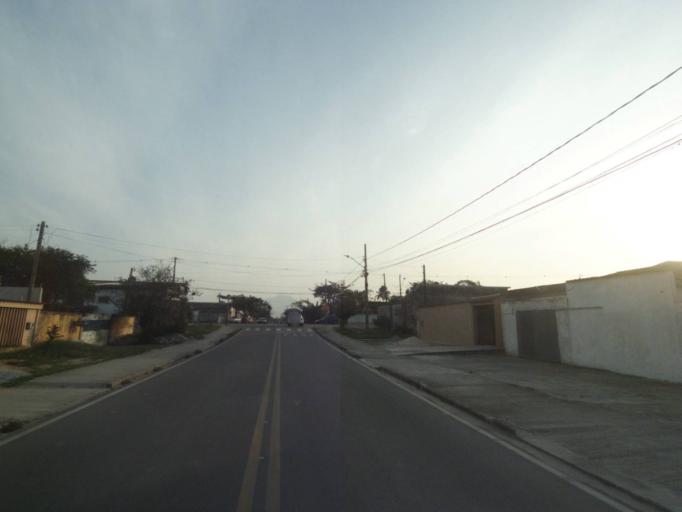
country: BR
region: Parana
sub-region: Paranagua
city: Paranagua
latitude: -25.5153
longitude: -48.5413
